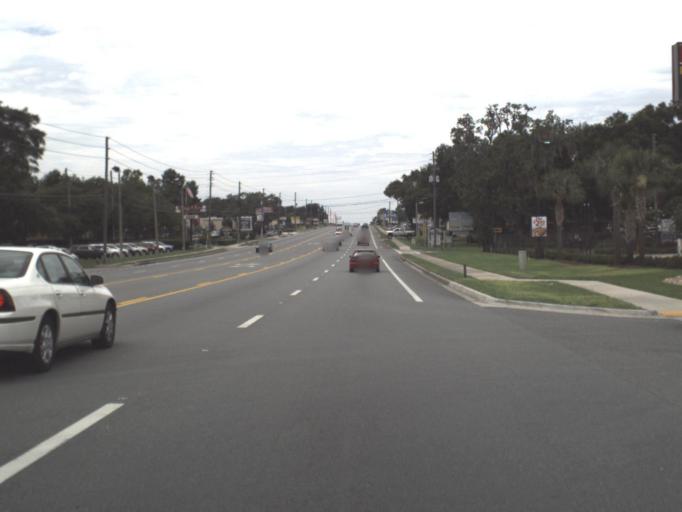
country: US
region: Florida
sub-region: Citrus County
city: Inverness
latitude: 28.8390
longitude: -82.3578
